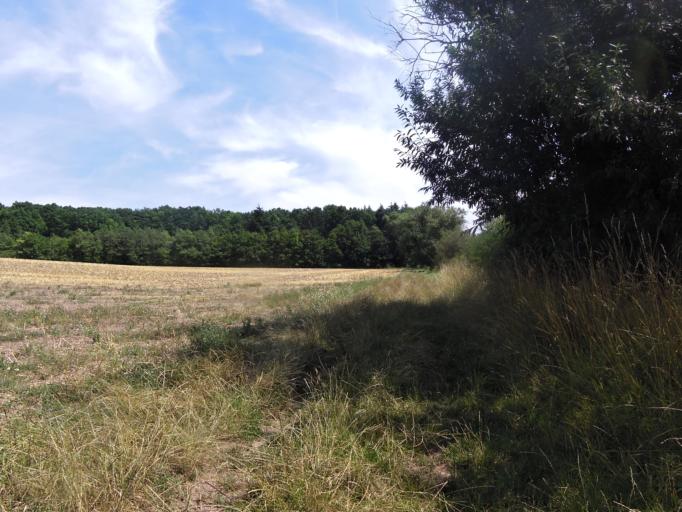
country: DE
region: Bavaria
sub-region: Regierungsbezirk Unterfranken
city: Estenfeld
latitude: 49.8071
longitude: 10.0099
